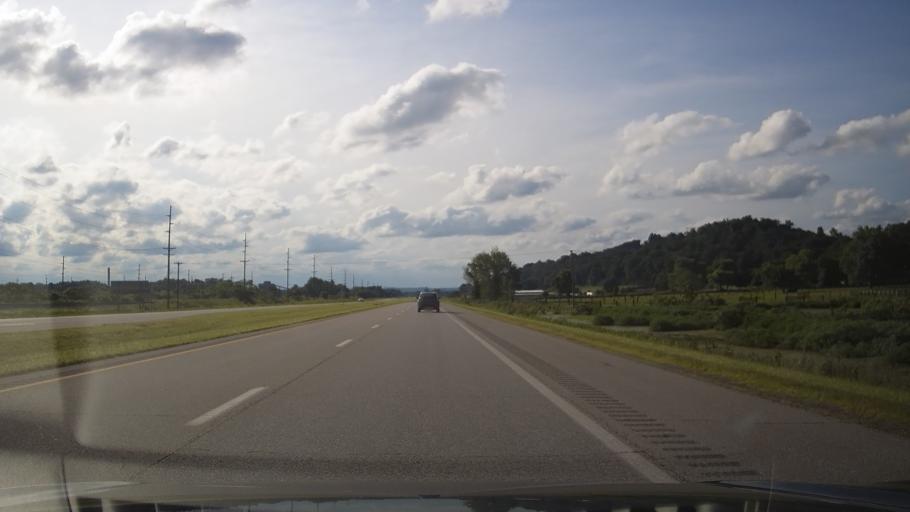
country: US
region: Kentucky
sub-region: Greenup County
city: Greenup
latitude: 38.5928
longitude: -82.8078
